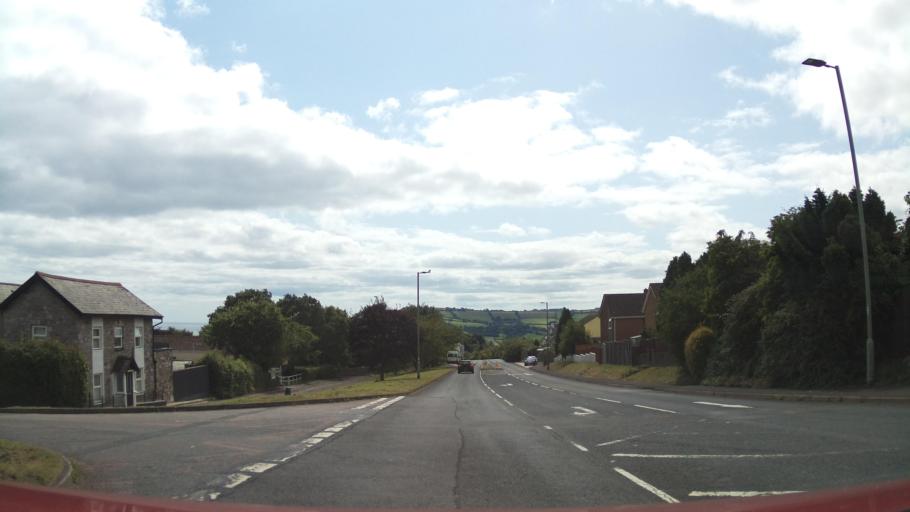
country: GB
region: England
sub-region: Devon
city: Teignmouth
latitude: 50.5598
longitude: -3.5047
